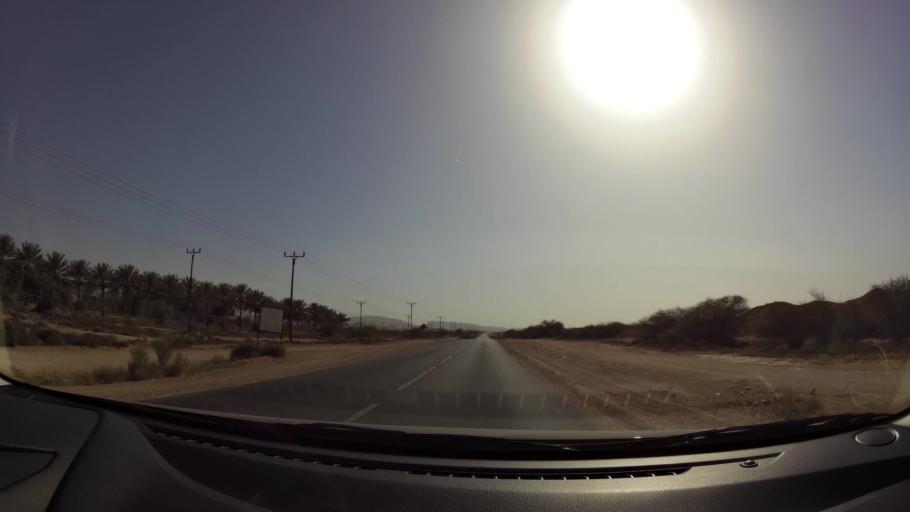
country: OM
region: Muhafazat Masqat
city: As Sib al Jadidah
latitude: 23.5801
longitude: 58.2334
